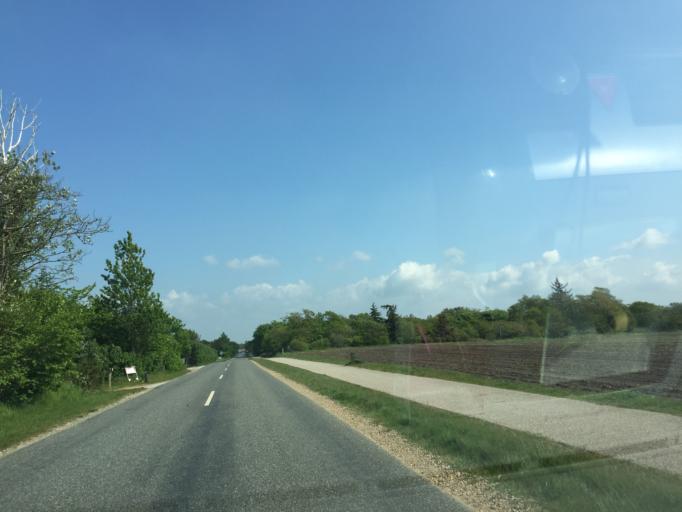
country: DK
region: South Denmark
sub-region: Esbjerg Kommune
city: Ribe
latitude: 55.2867
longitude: 8.7110
